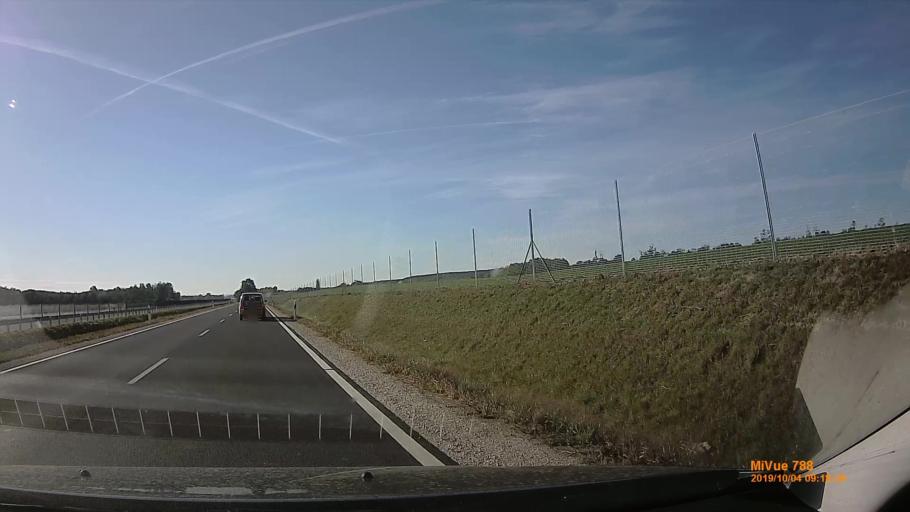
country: HU
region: Somogy
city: Karad
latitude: 46.5887
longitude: 17.8026
